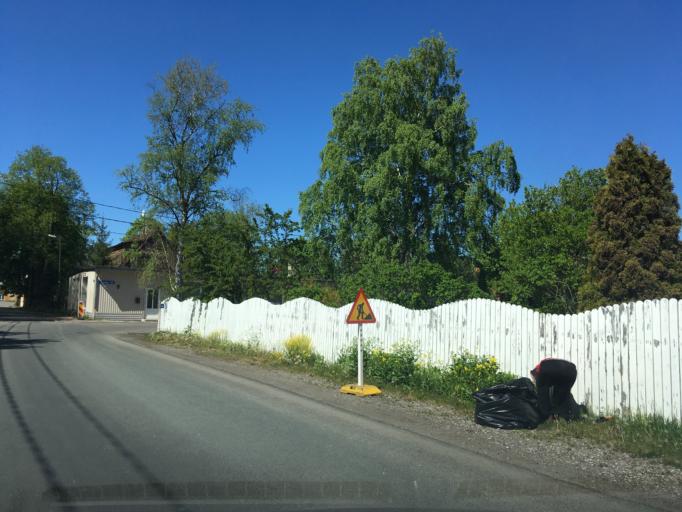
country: EE
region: Harju
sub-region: Tallinna linn
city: Tallinn
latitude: 59.4130
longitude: 24.7488
